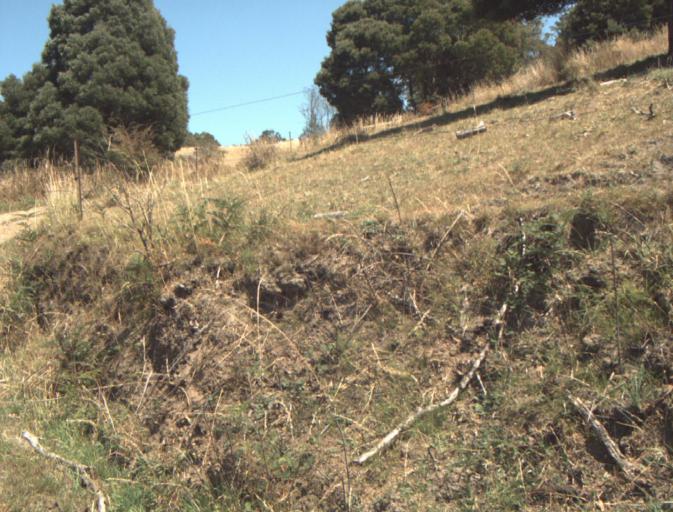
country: AU
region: Tasmania
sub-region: Launceston
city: Mayfield
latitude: -41.2717
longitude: 147.1230
